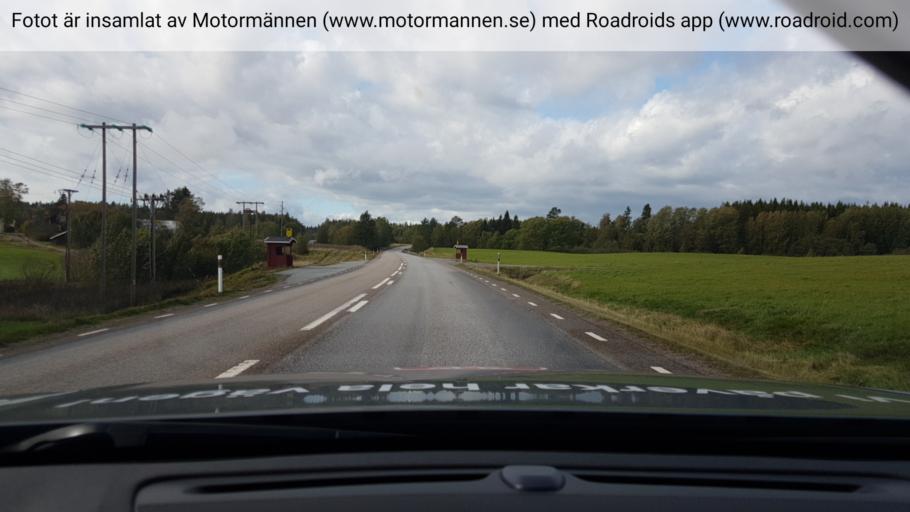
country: SE
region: Vaermland
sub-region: Arjangs Kommun
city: Arjaeng
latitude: 59.4685
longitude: 11.9988
